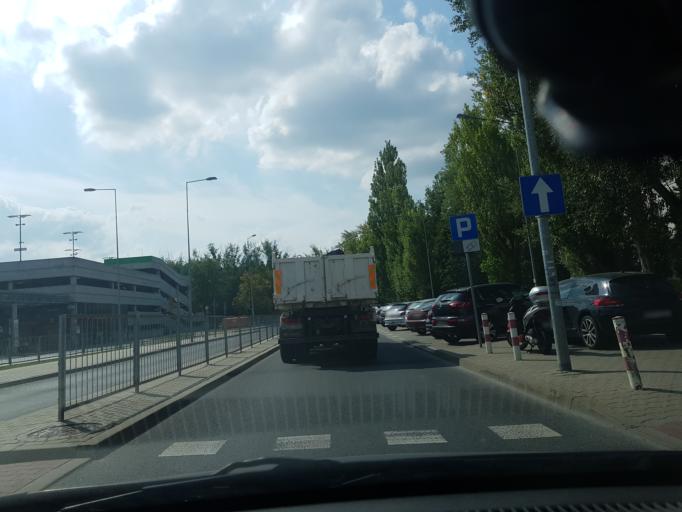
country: PL
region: Masovian Voivodeship
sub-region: Warszawa
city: Bielany
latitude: 52.2917
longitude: 20.9274
